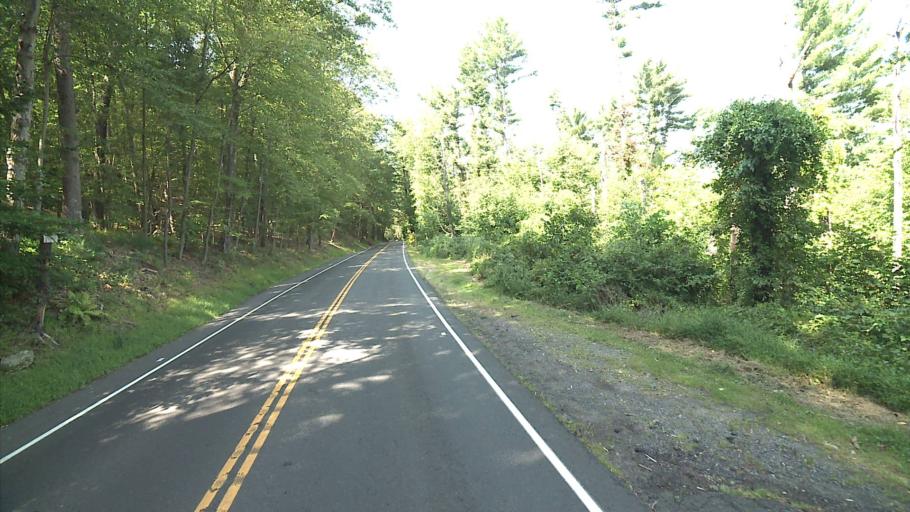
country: US
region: Connecticut
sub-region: Fairfield County
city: Southport
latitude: 41.2187
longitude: -73.2973
